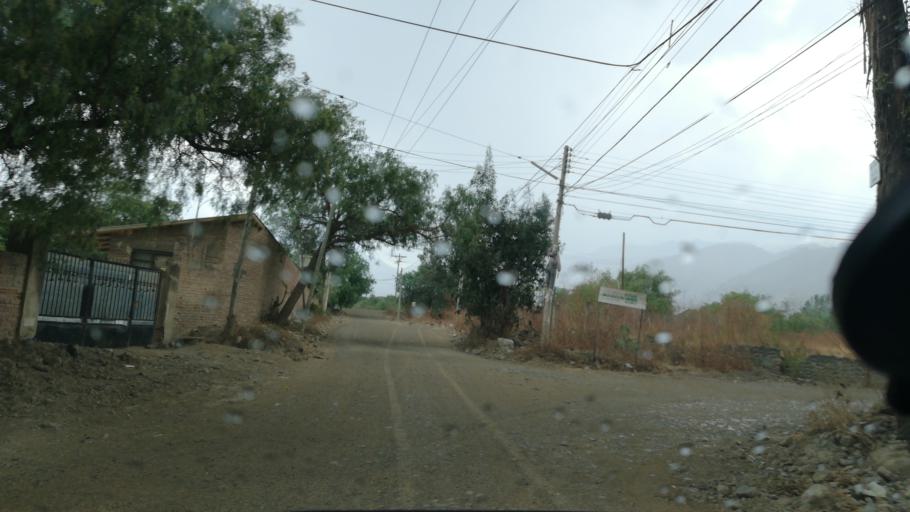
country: BO
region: Cochabamba
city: Cochabamba
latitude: -17.3381
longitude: -66.2100
